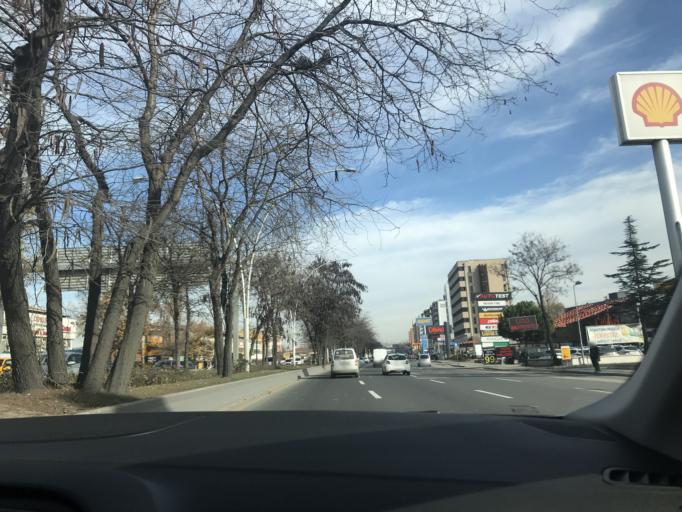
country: TR
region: Ankara
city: Ankara
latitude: 39.9535
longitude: 32.8387
